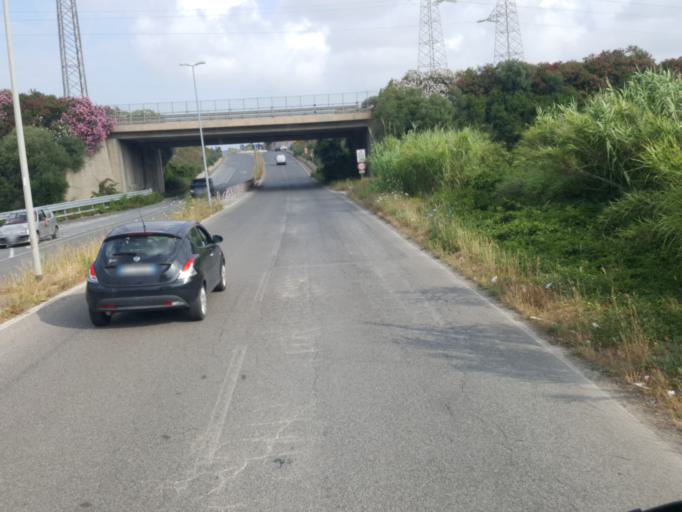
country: IT
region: Latium
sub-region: Citta metropolitana di Roma Capitale
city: Civitavecchia
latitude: 42.1055
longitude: 11.7905
